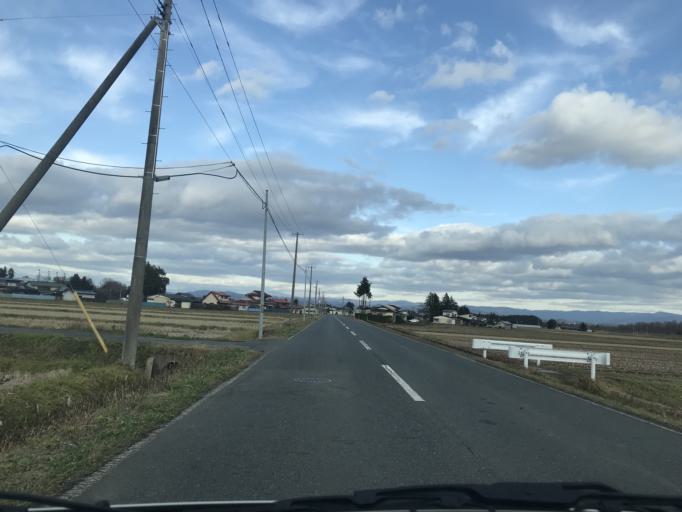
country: JP
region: Iwate
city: Mizusawa
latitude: 39.1704
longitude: 141.0886
